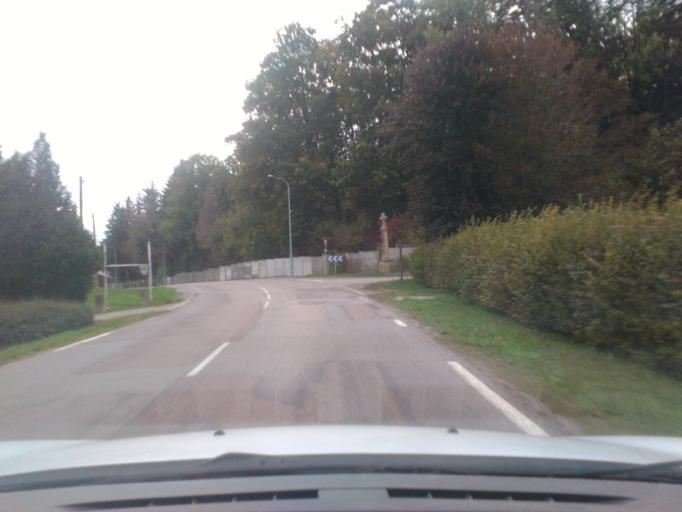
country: FR
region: Lorraine
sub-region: Departement des Vosges
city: Rambervillers
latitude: 48.3569
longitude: 6.5905
